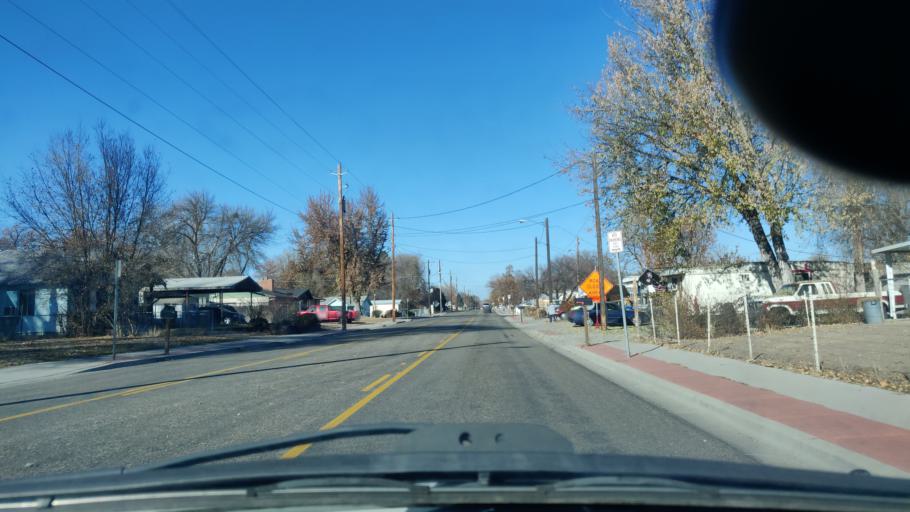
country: US
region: Idaho
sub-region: Ada County
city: Garden City
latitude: 43.6376
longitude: -116.2514
